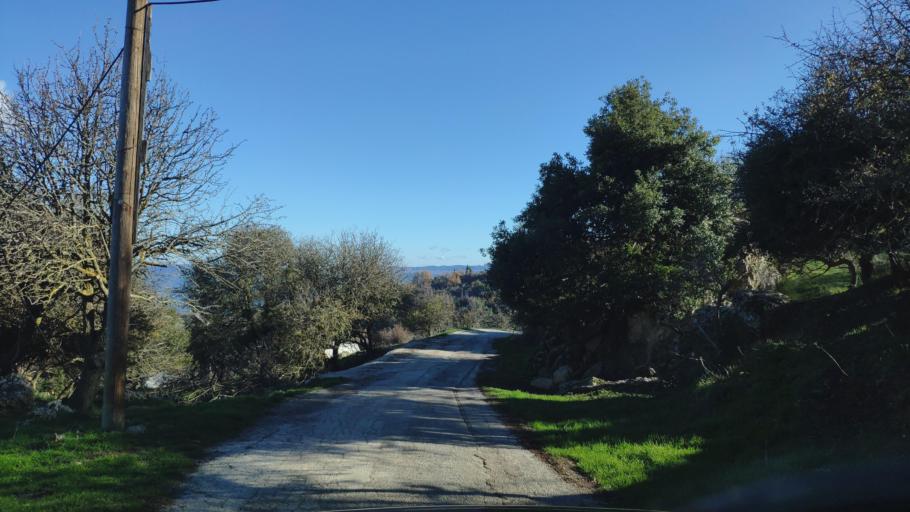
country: GR
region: West Greece
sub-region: Nomos Achaias
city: Aiyira
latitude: 38.0384
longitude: 22.4669
